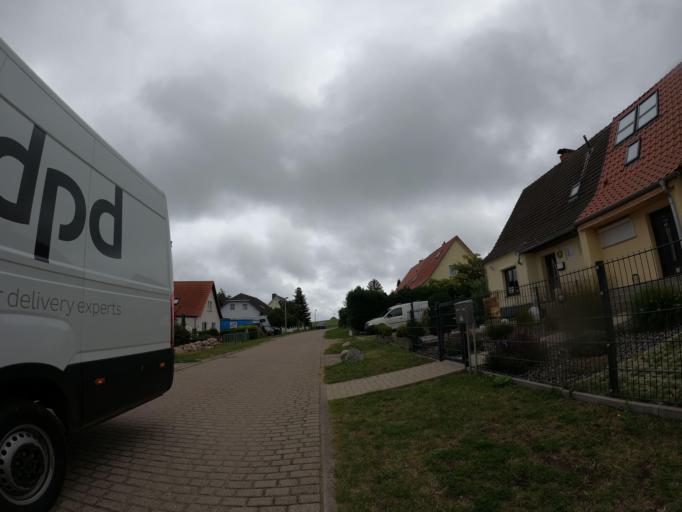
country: DE
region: Mecklenburg-Vorpommern
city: Ostseebad Gohren
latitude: 54.3072
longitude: 13.6878
